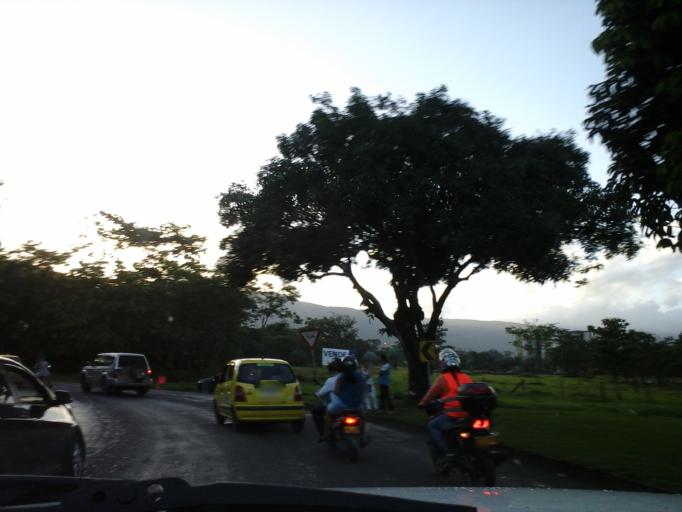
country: CO
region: Meta
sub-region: Villavicencio
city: Villavicencio
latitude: 4.1234
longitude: -73.6408
